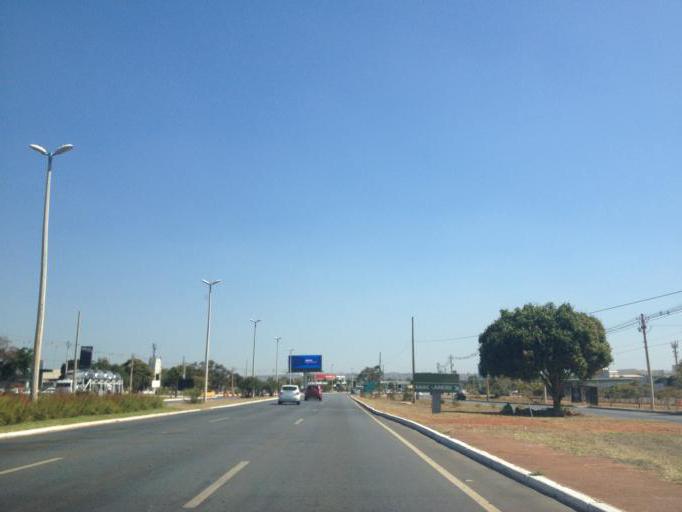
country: BR
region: Federal District
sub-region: Brasilia
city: Brasilia
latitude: -15.8705
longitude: -47.9317
